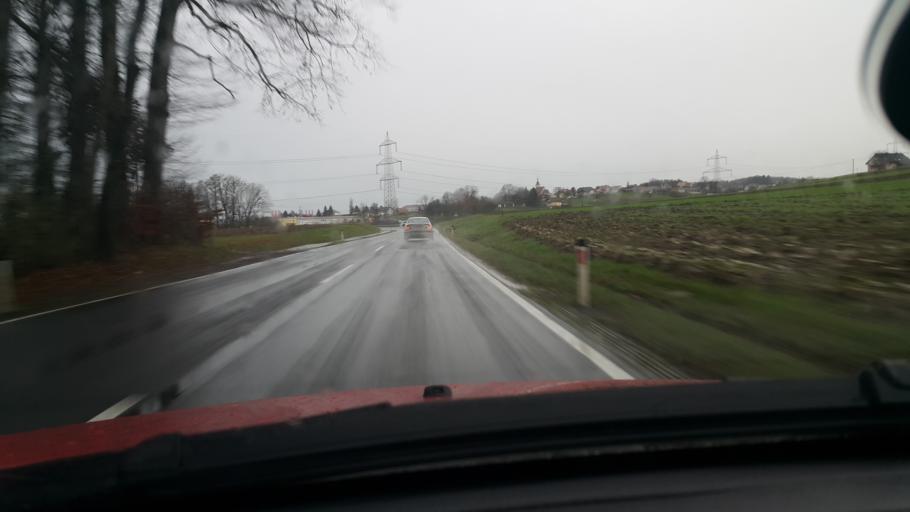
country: AT
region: Styria
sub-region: Politischer Bezirk Deutschlandsberg
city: Preding
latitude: 46.8523
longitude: 15.4181
